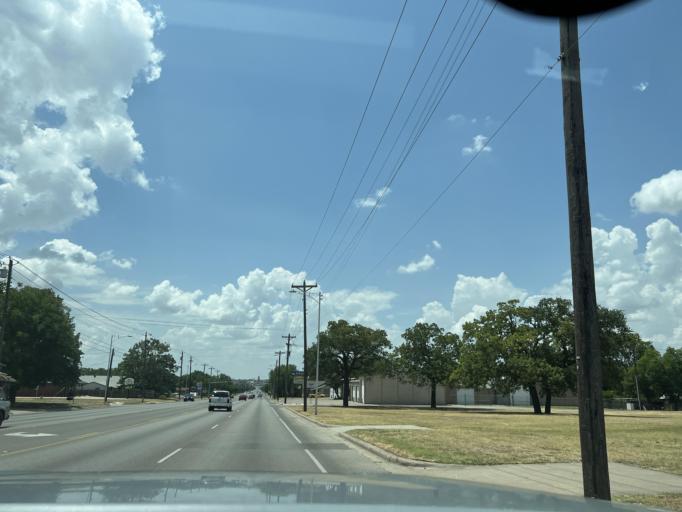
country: US
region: Texas
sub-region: Parker County
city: Weatherford
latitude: 32.7759
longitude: -97.7973
